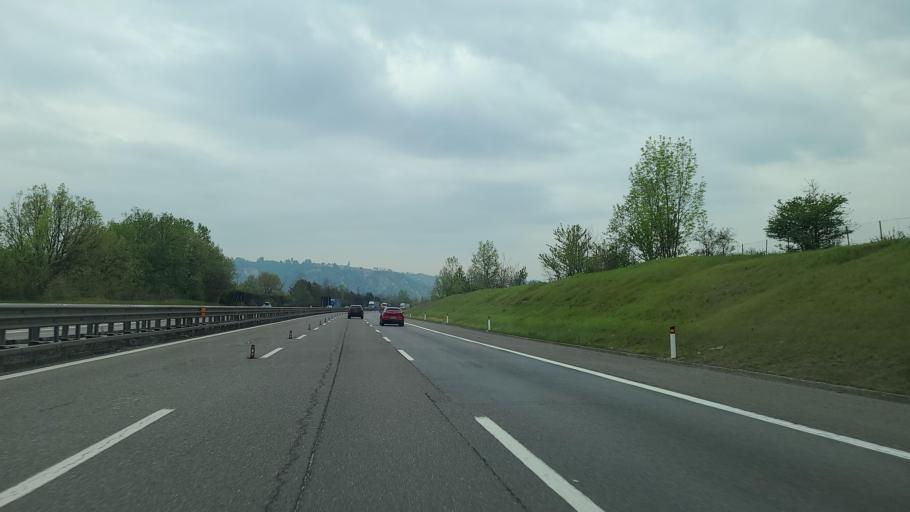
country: IT
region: Piedmont
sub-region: Provincia di Alessandria
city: Tagliolo Monferrato
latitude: 44.6513
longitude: 8.6612
